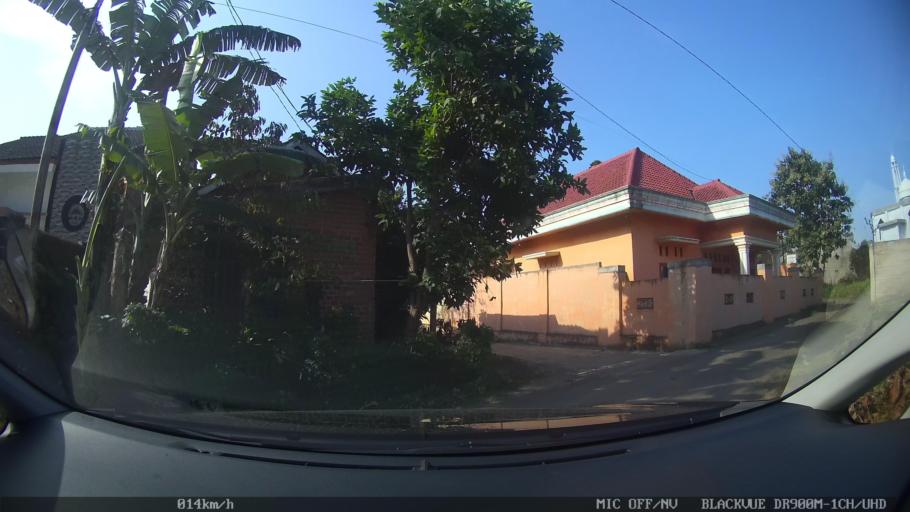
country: ID
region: Lampung
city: Kedaton
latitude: -5.3766
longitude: 105.2314
